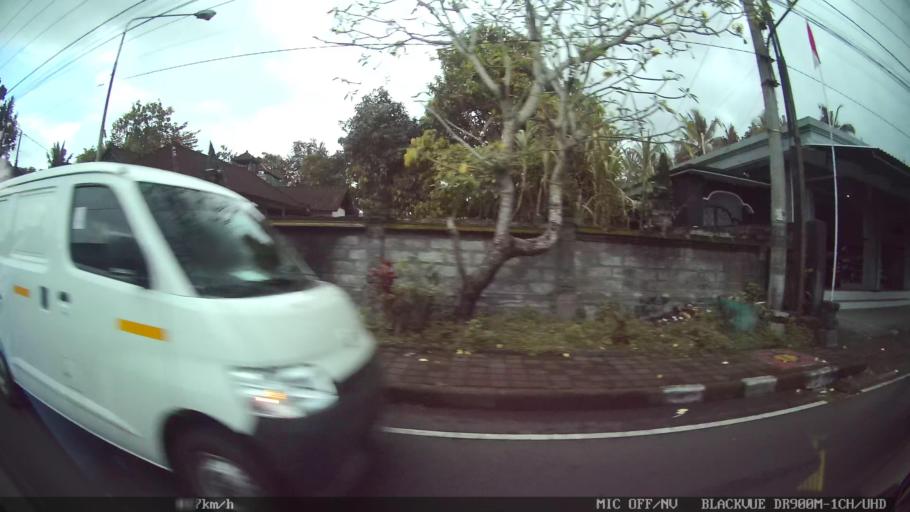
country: ID
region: Bali
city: Banjar Sempidi
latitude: -8.5300
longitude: 115.2010
